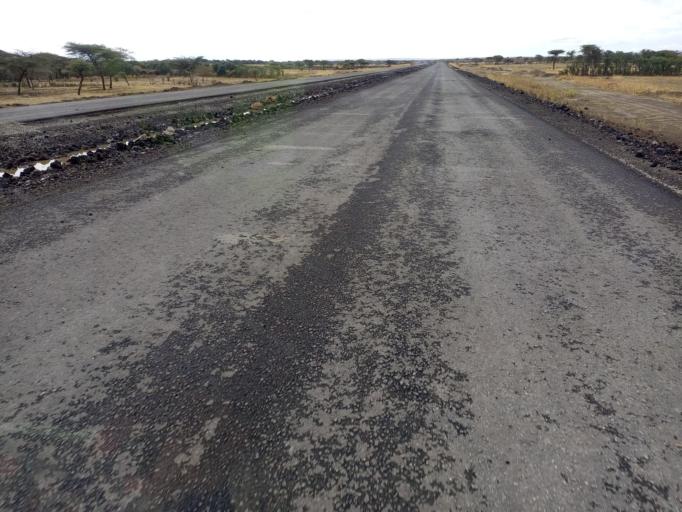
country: ET
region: Oromiya
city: Ziway
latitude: 7.6341
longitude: 38.6806
